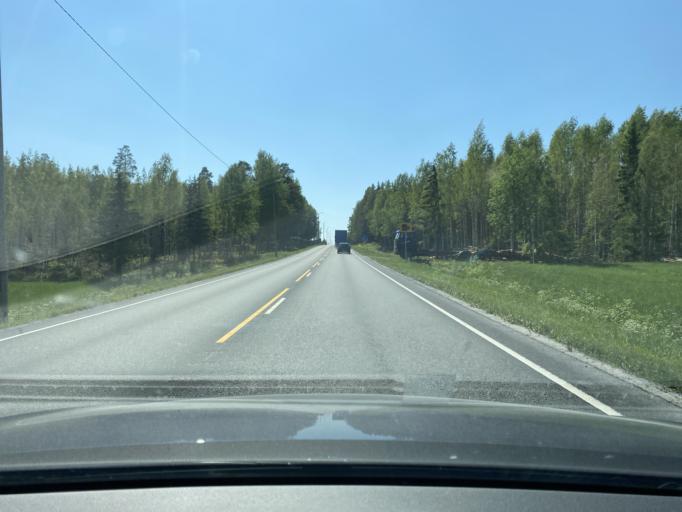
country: FI
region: Pirkanmaa
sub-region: Lounais-Pirkanmaa
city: Mouhijaervi
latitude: 61.3583
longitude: 23.0883
